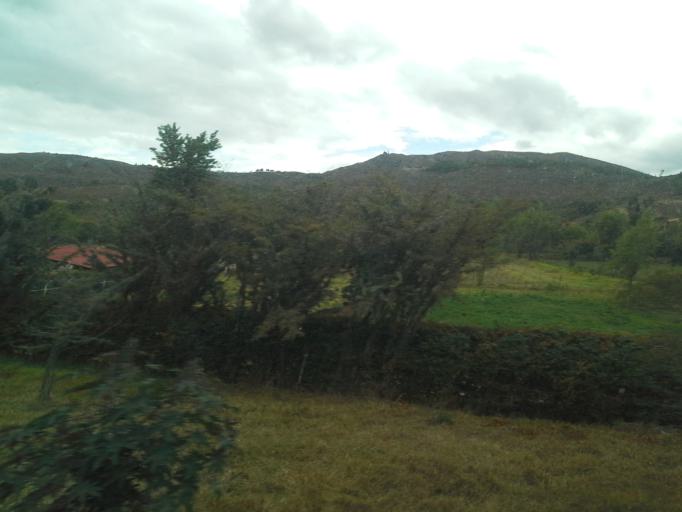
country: CO
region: Boyaca
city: Raquira
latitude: 5.5557
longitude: -73.6421
